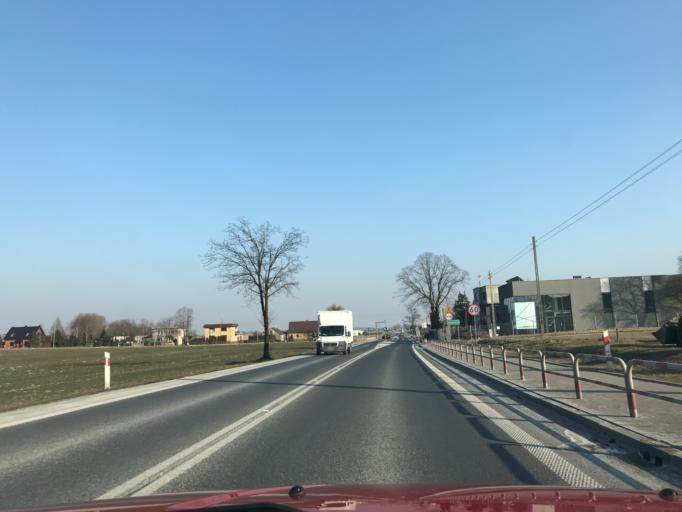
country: PL
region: Greater Poland Voivodeship
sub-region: Powiat pleszewski
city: Pleszew
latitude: 51.8933
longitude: 17.8204
